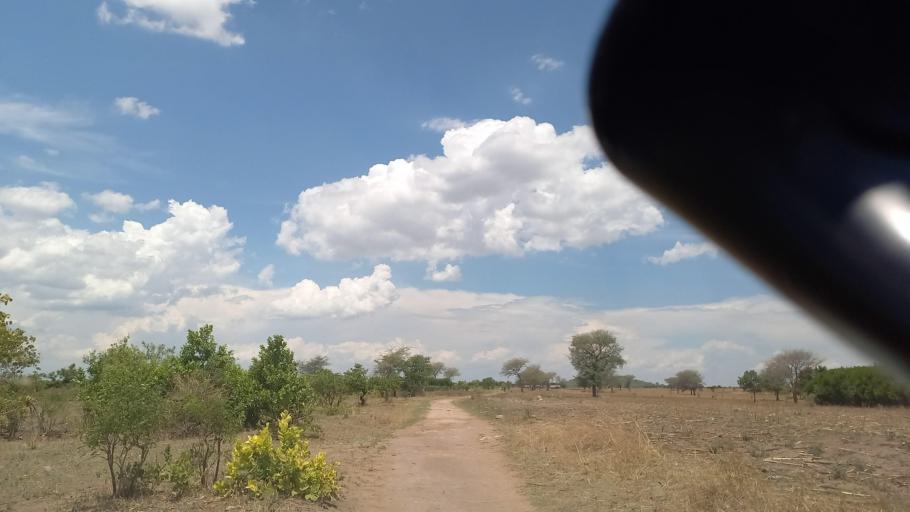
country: ZM
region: Southern
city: Mazabuka
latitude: -16.1097
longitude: 27.8184
